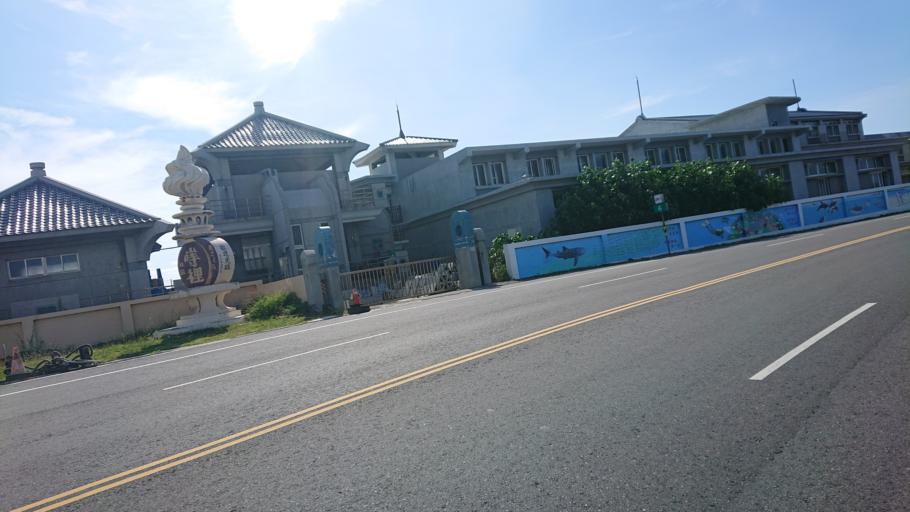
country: TW
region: Taiwan
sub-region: Penghu
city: Ma-kung
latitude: 23.5199
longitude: 119.5739
